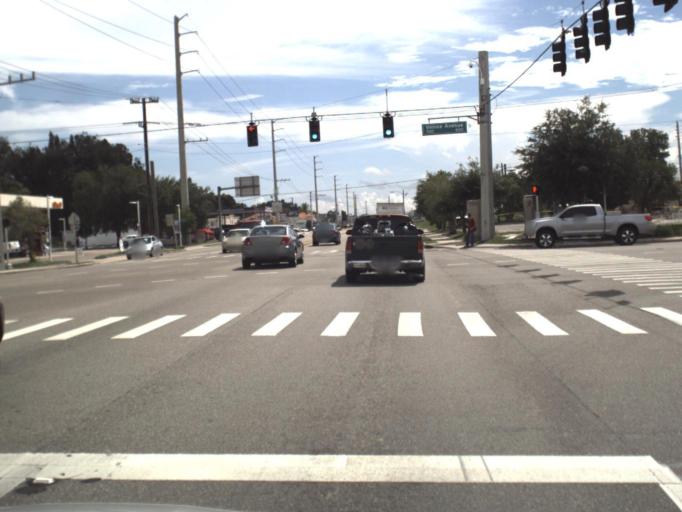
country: US
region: Florida
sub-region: Sarasota County
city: Venice
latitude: 27.1001
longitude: -82.4336
